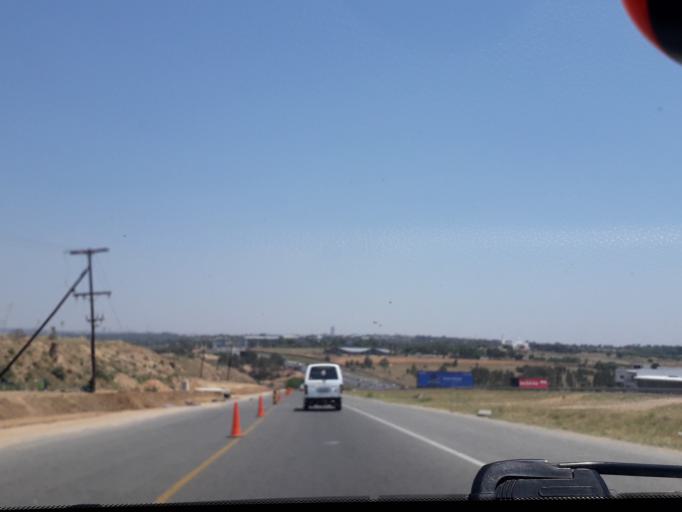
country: ZA
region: Gauteng
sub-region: City of Johannesburg Metropolitan Municipality
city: Midrand
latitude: -26.0258
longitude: 28.1135
